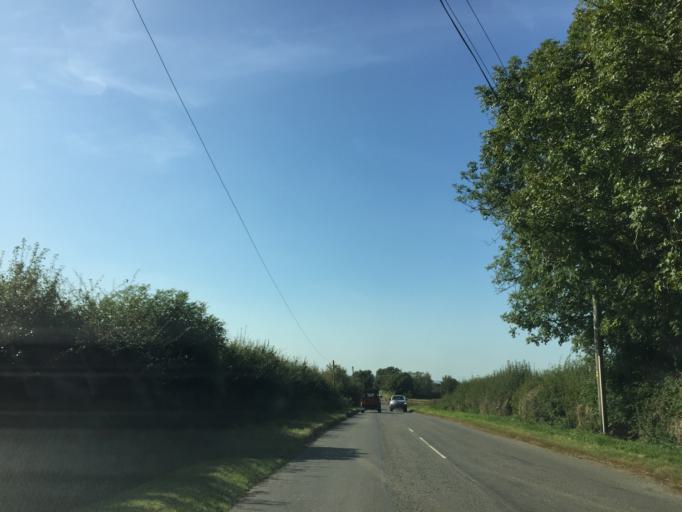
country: GB
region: England
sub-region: Leicestershire
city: Queniborough
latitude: 52.7002
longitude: -1.0186
